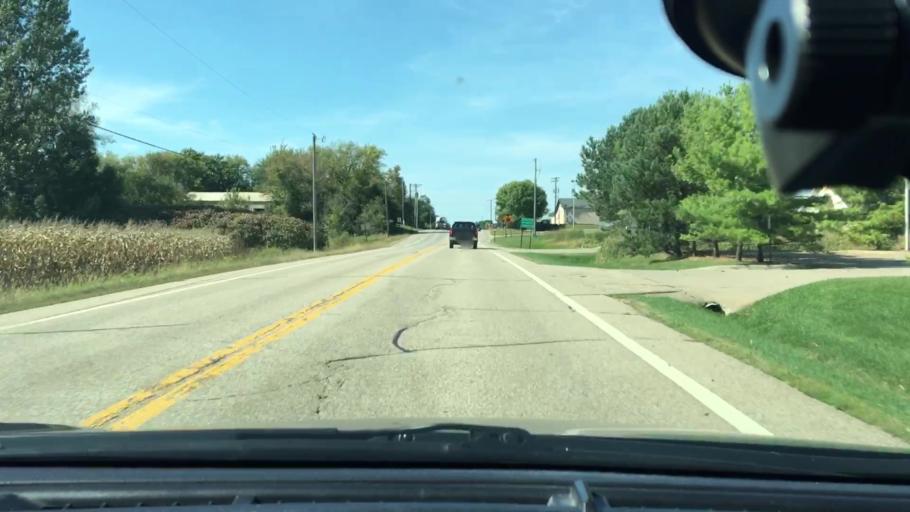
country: US
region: Minnesota
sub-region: Wright County
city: Hanover
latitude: 45.1236
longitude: -93.6315
